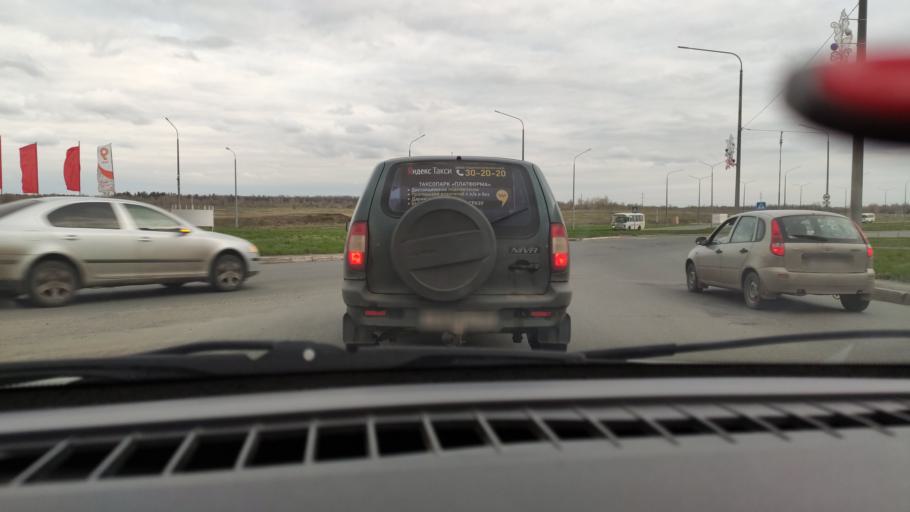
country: RU
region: Orenburg
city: Orenburg
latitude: 51.8105
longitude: 55.1795
